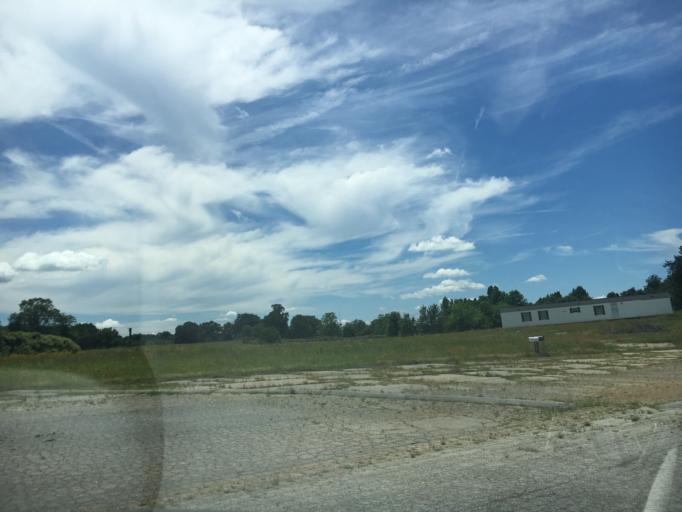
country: US
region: South Carolina
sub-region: Spartanburg County
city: Duncan
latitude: 34.8529
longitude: -82.1503
